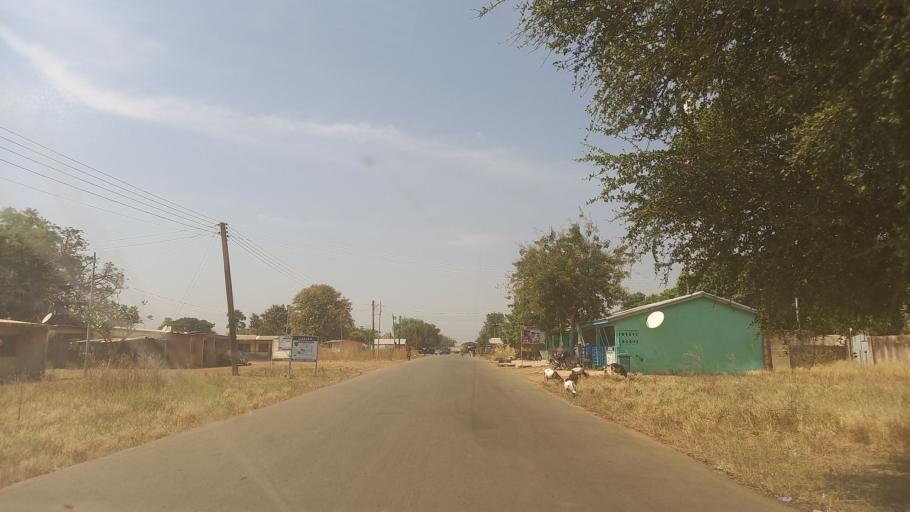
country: GH
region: Upper East
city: Navrongo
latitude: 10.8825
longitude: -1.0822
